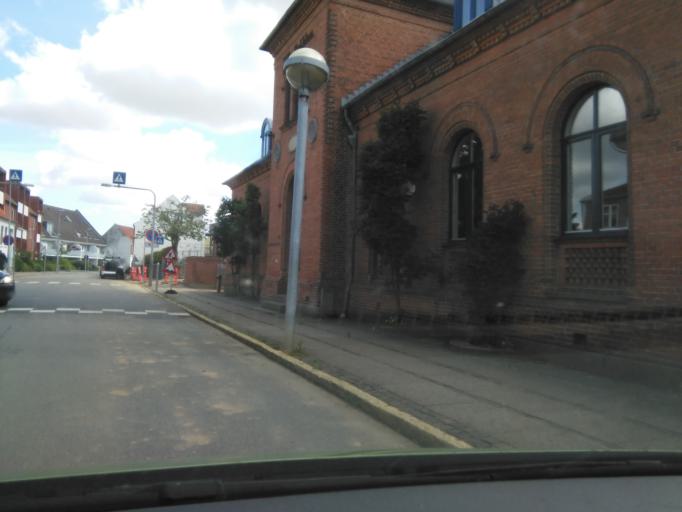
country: DK
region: Central Jutland
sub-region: Odder Kommune
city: Odder
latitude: 55.9703
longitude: 10.1397
